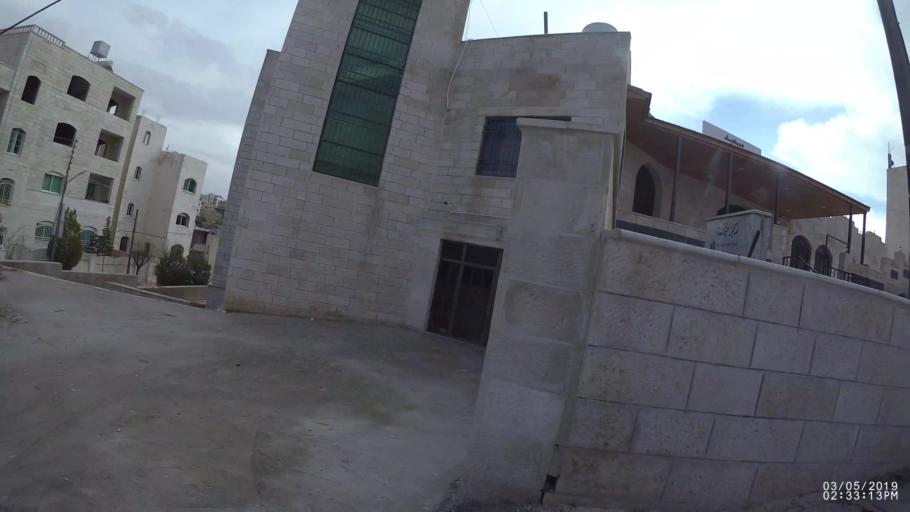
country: JO
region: Amman
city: Amman
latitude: 32.0116
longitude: 35.9460
